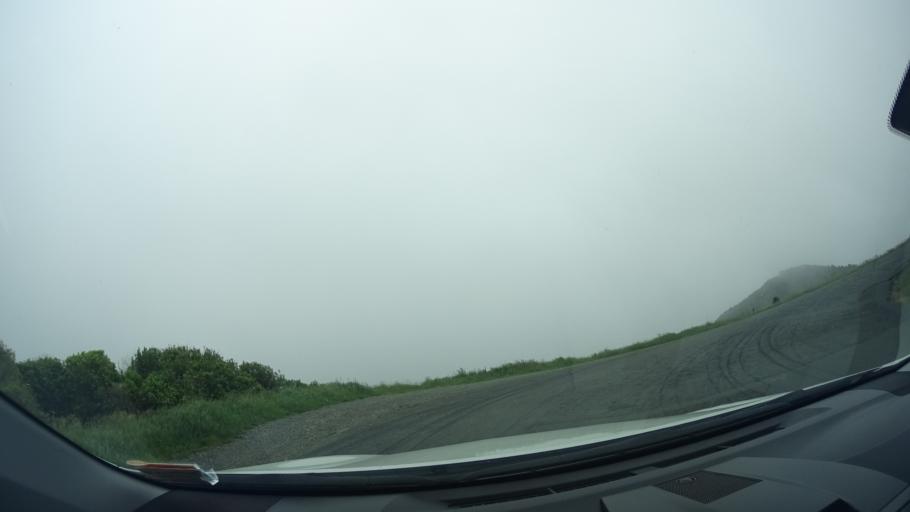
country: NZ
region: Wellington
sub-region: Wellington City
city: Brooklyn
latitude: -41.3112
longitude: 174.7460
